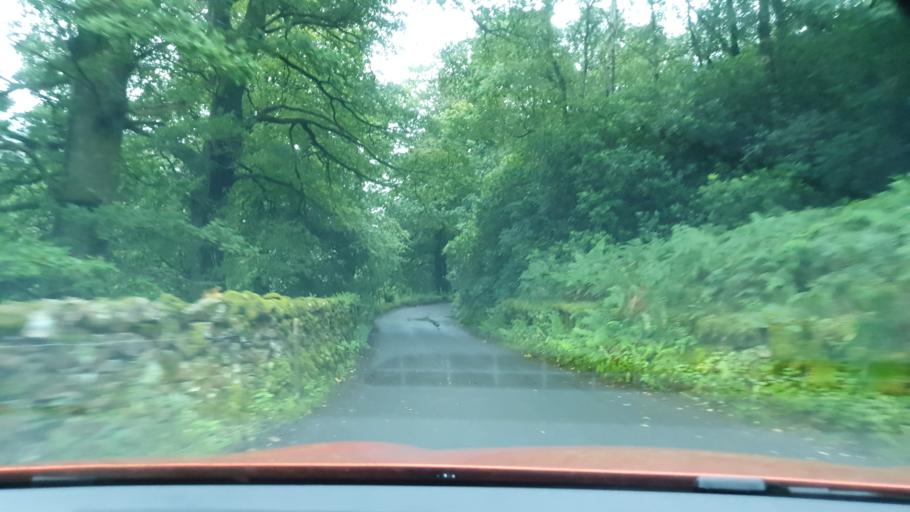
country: GB
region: England
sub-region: Cumbria
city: Seascale
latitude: 54.4308
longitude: -3.3177
